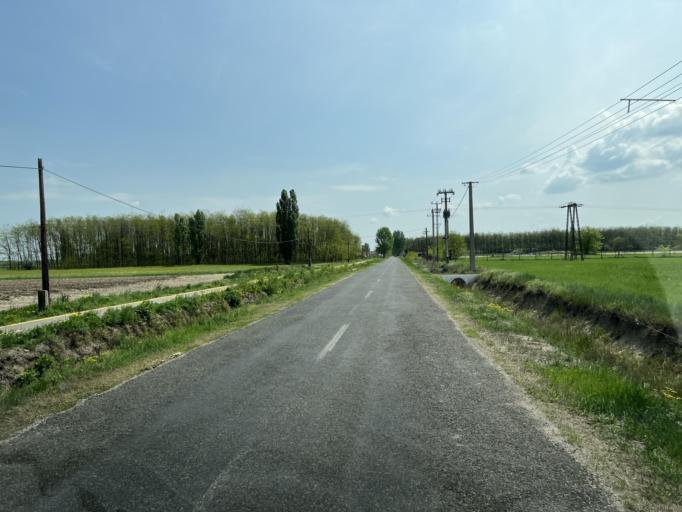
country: HU
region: Pest
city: Nagykoros
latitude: 47.0983
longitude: 19.8123
